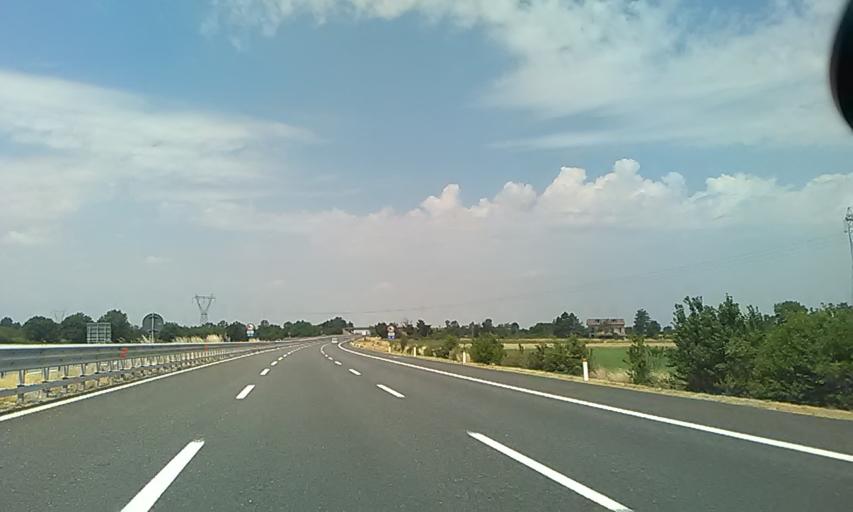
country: IT
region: Piedmont
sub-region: Provincia di Alessandria
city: Predosa
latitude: 44.7650
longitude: 8.6364
